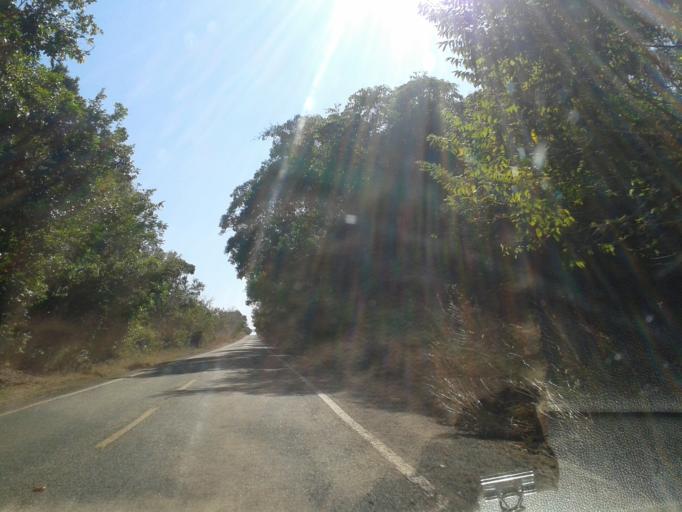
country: BR
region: Goias
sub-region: Mozarlandia
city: Mozarlandia
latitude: -14.4857
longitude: -50.4792
